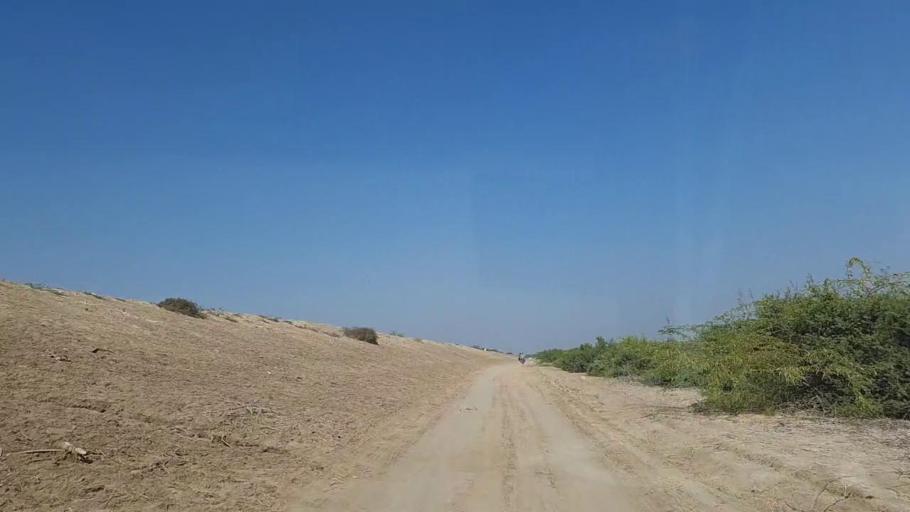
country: PK
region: Sindh
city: Chuhar Jamali
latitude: 24.4710
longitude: 68.0076
